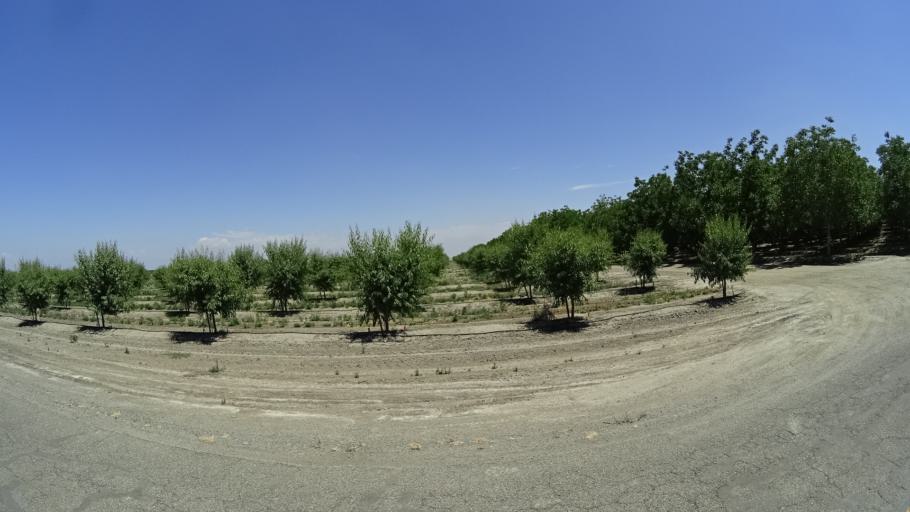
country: US
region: California
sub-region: Kings County
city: Lucerne
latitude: 36.4051
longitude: -119.6189
